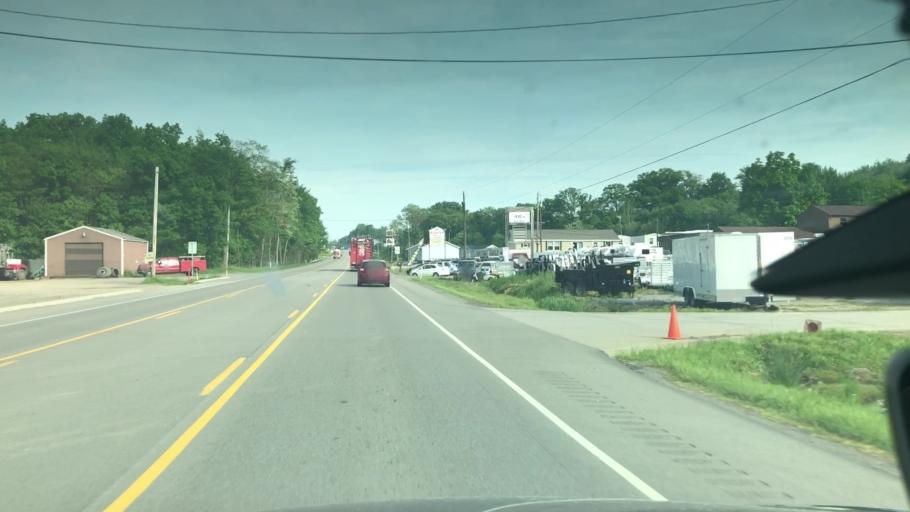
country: US
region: Pennsylvania
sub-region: Butler County
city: Prospect
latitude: 40.8992
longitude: -80.0093
